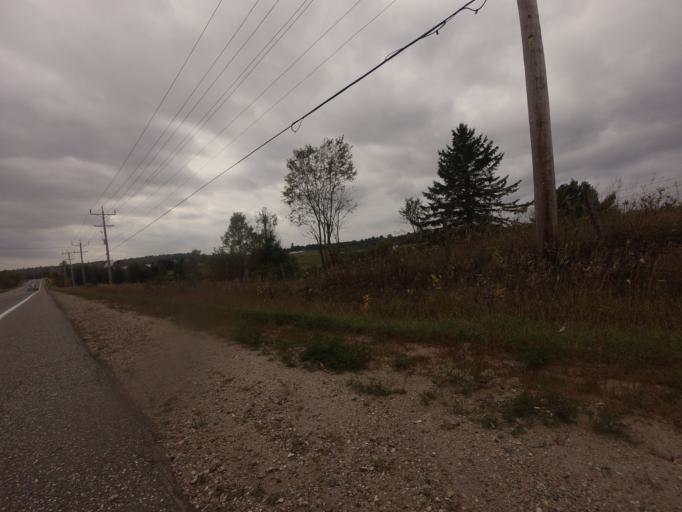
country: CA
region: Quebec
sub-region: Outaouais
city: Wakefield
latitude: 45.9188
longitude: -76.0174
